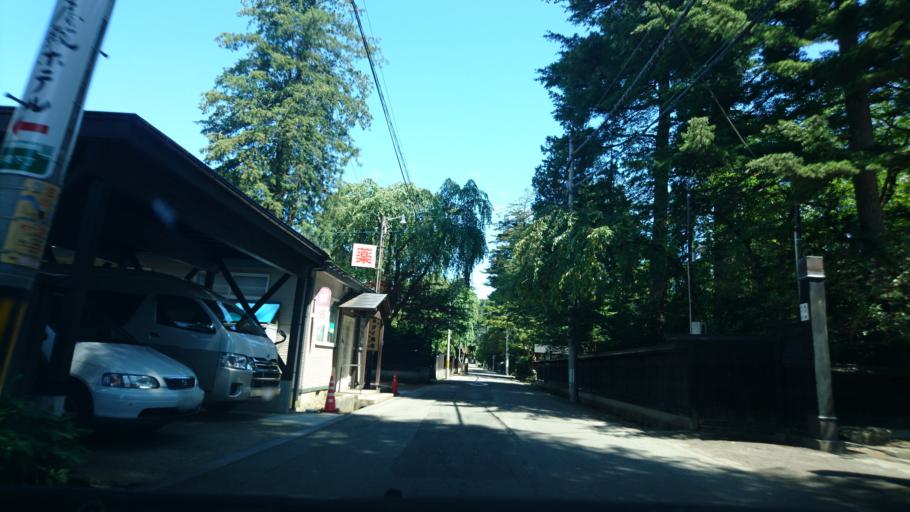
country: JP
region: Akita
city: Kakunodatemachi
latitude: 39.5910
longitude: 140.5650
